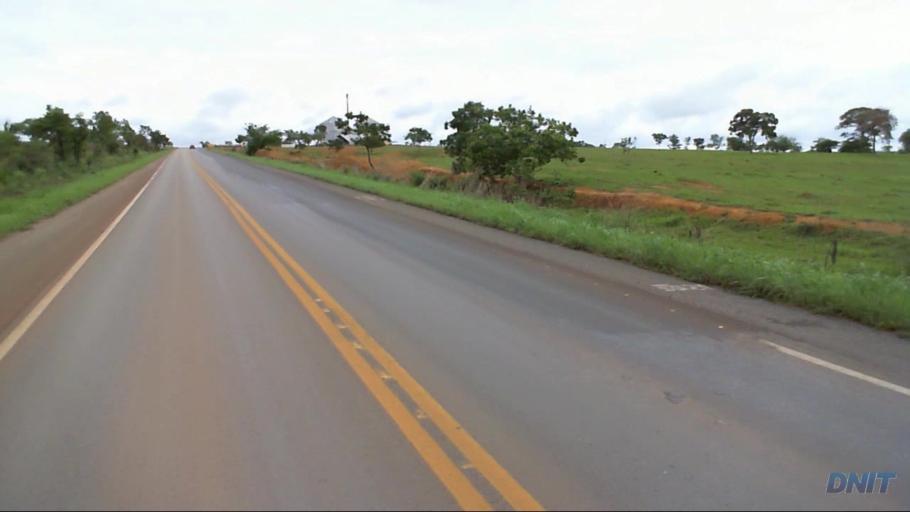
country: BR
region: Goias
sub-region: Padre Bernardo
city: Padre Bernardo
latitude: -15.1564
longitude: -48.3226
